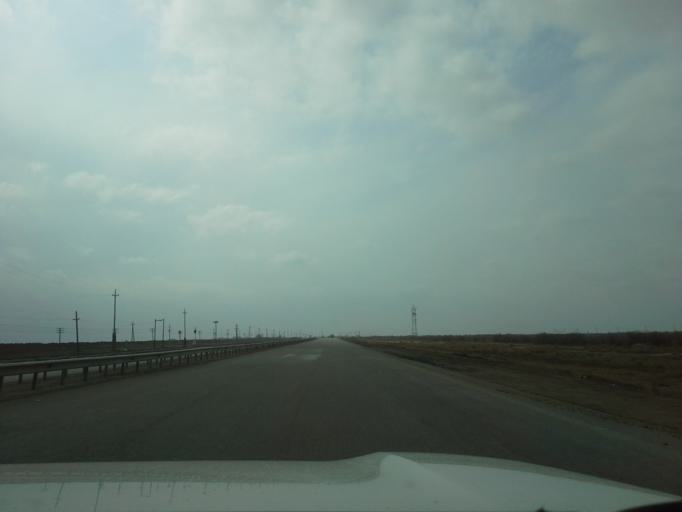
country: IR
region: Razavi Khorasan
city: Kalat-e Naderi
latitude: 37.2062
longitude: 60.0544
